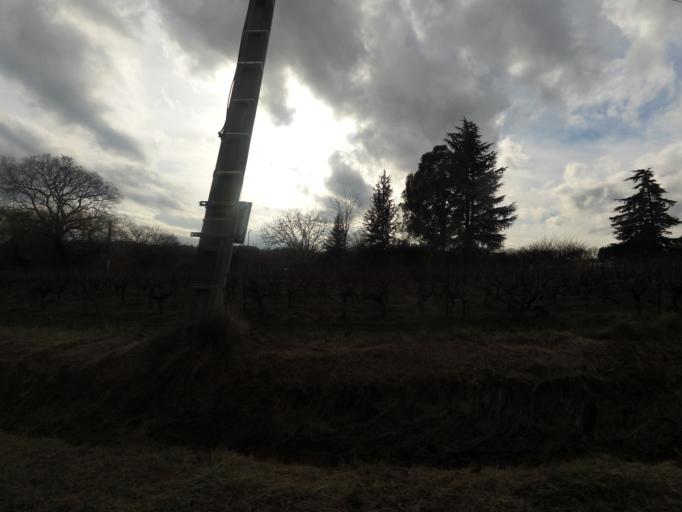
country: FR
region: Languedoc-Roussillon
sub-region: Departement du Gard
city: Saint-Mamert-du-Gard
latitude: 43.9022
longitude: 4.2164
